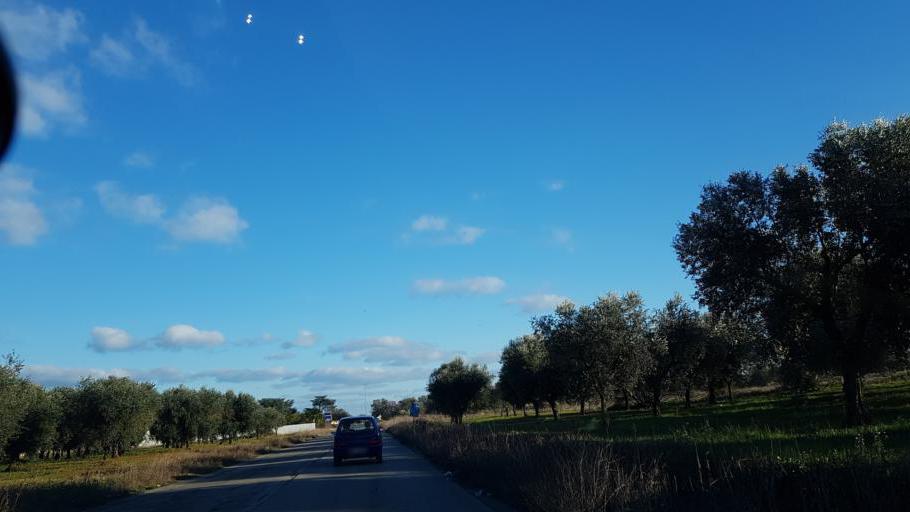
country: IT
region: Apulia
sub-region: Provincia di Brindisi
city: San Pietro Vernotico
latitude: 40.4783
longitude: 18.0027
